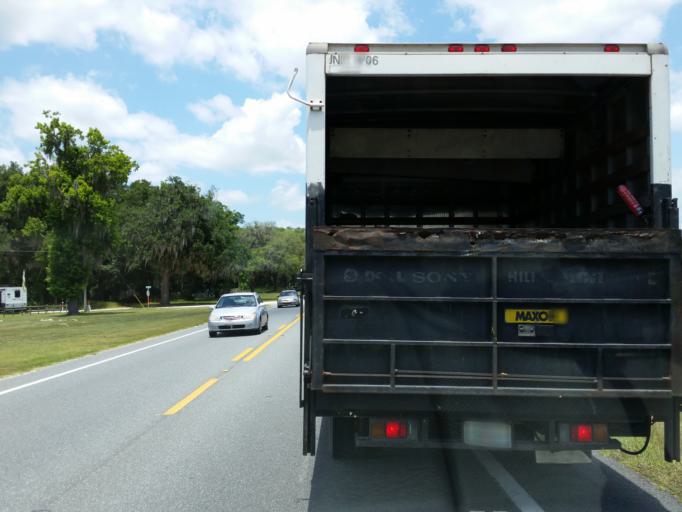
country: US
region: Florida
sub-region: Marion County
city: Belleview
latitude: 29.0014
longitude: -82.0413
